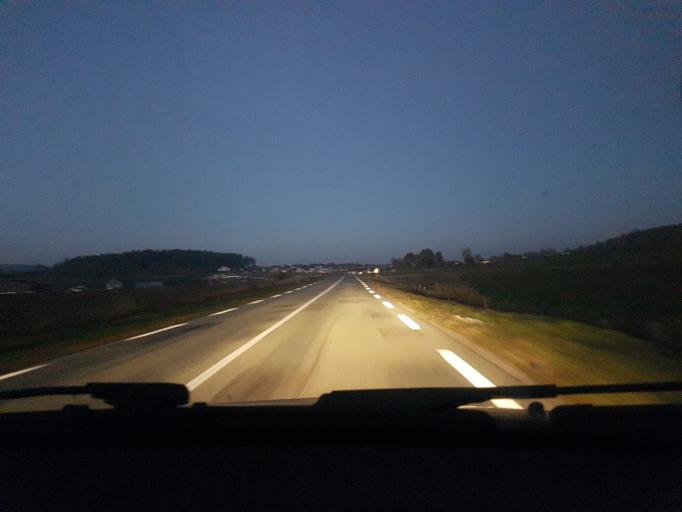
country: FR
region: Franche-Comte
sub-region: Departement du Doubs
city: Les Fins
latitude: 47.0946
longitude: 6.6495
